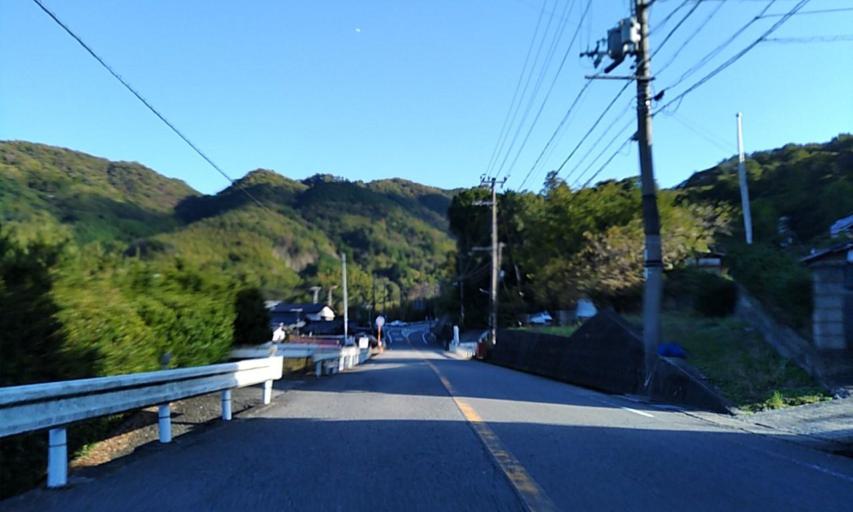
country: JP
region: Wakayama
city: Iwade
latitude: 34.1539
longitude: 135.3191
